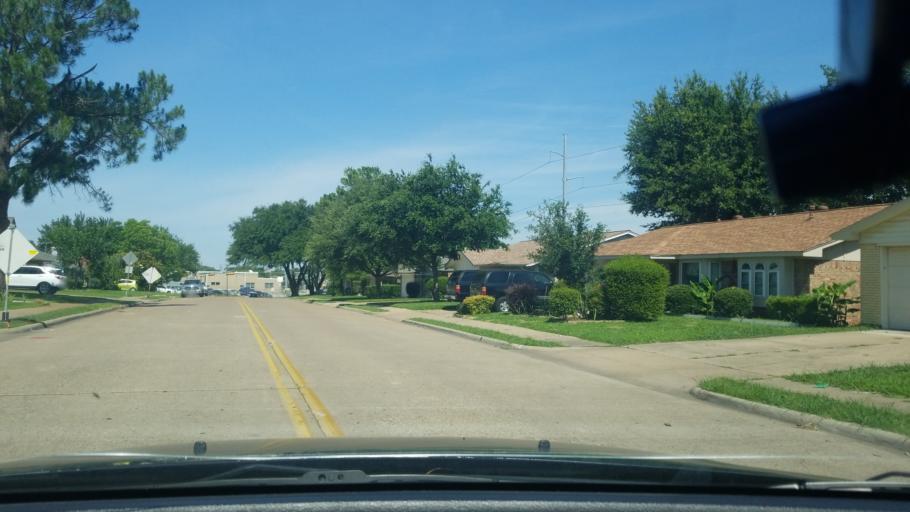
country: US
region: Texas
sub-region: Dallas County
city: Mesquite
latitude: 32.7752
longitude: -96.5953
